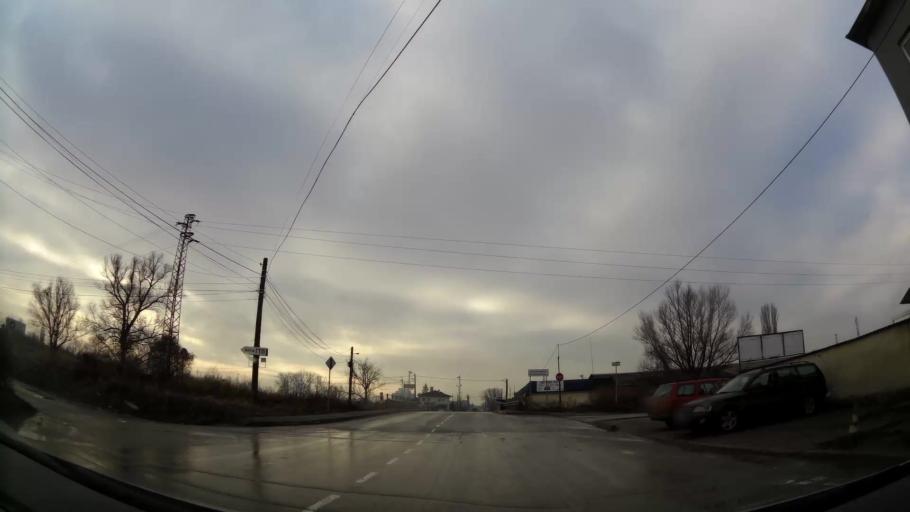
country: BG
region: Sofia-Capital
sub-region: Stolichna Obshtina
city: Sofia
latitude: 42.7336
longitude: 23.3434
